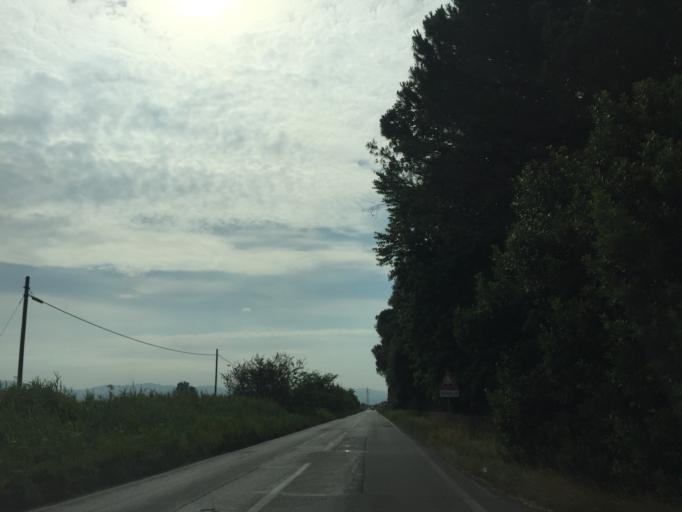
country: IT
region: Tuscany
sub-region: Provincia di Pistoia
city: Montecatini-Terme
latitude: 43.8545
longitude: 10.7801
